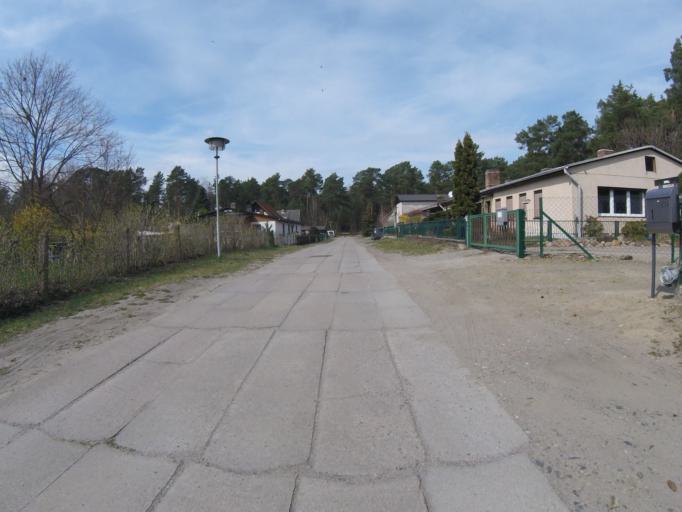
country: DE
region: Brandenburg
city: Gross Koris
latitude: 52.1708
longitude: 13.6494
